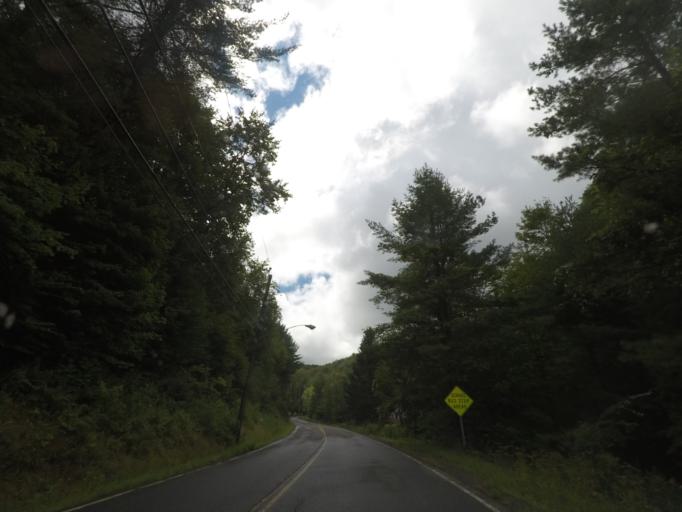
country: US
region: New York
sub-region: Rensselaer County
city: Averill Park
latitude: 42.6859
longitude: -73.3828
